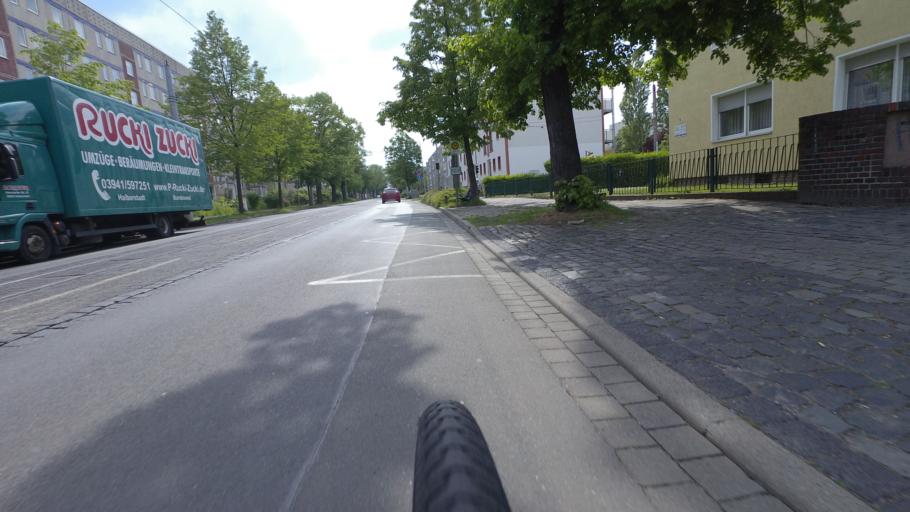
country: DE
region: Saxony-Anhalt
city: Halberstadt
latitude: 51.8968
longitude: 11.0679
